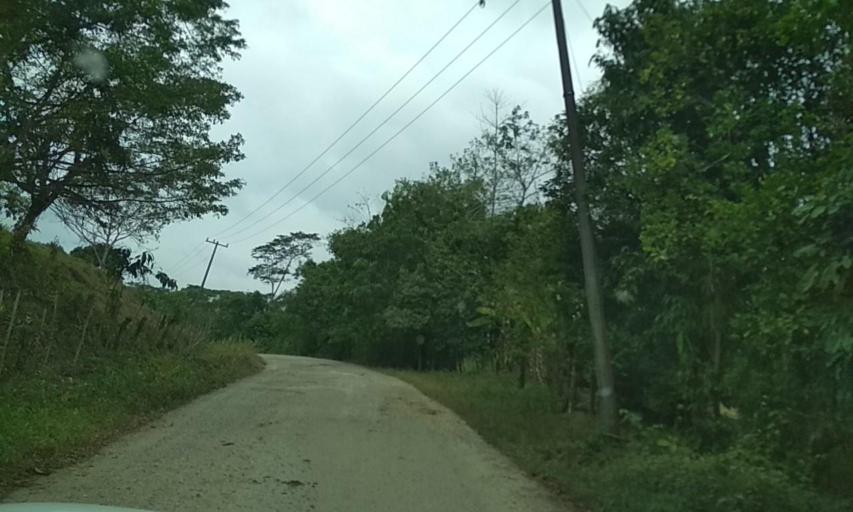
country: MX
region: Tabasco
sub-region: Huimanguillo
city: Francisco Rueda
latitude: 17.4962
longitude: -94.1320
